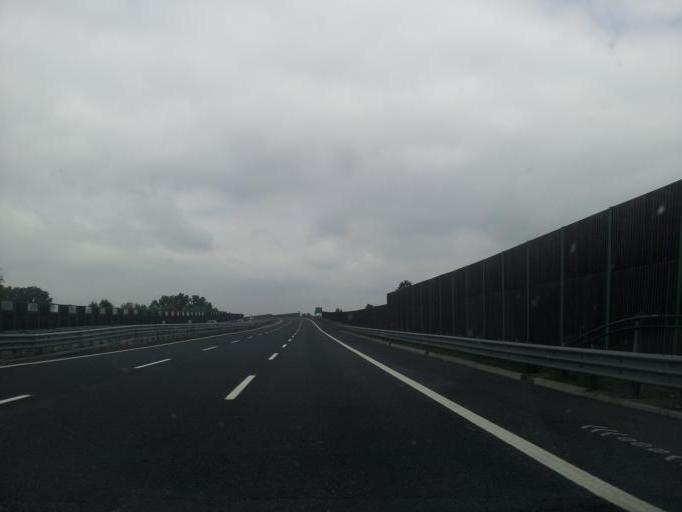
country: IT
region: Veneto
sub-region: Provincia di Venezia
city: Maerne
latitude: 45.5141
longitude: 12.1399
